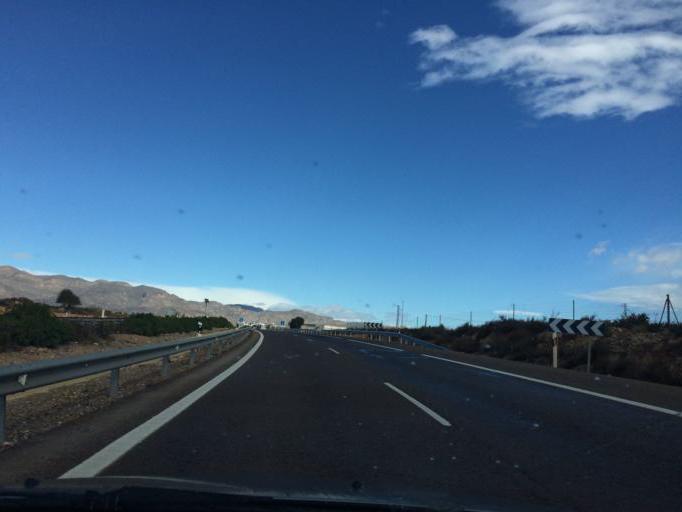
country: ES
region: Andalusia
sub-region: Provincia de Almeria
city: Nijar
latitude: 36.8908
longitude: -2.2137
